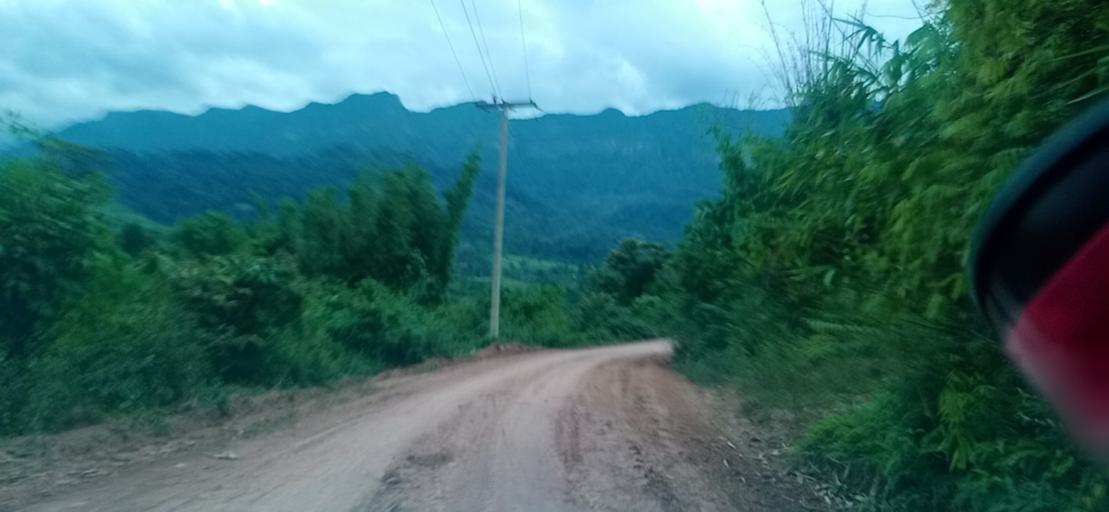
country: TH
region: Changwat Bueng Kan
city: Pak Khat
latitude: 18.5513
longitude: 103.4257
